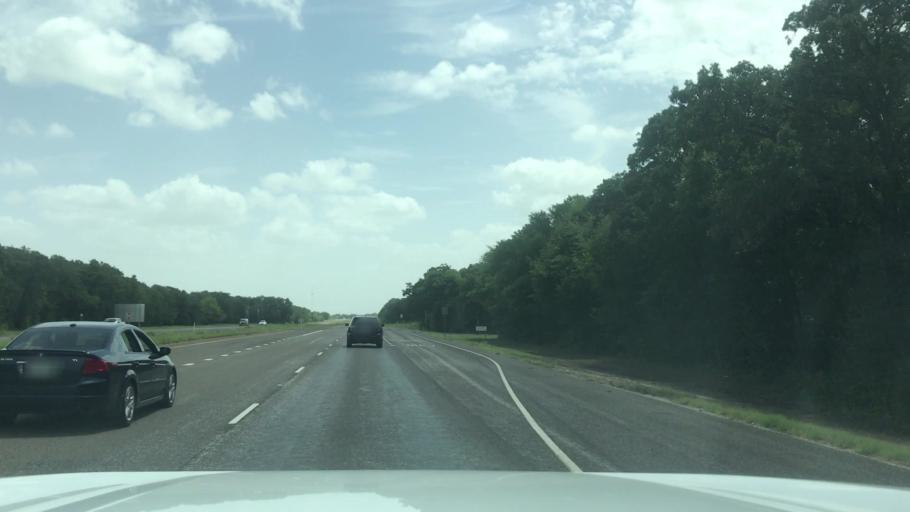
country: US
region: Texas
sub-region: Falls County
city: Marlin
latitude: 31.2959
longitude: -96.8751
